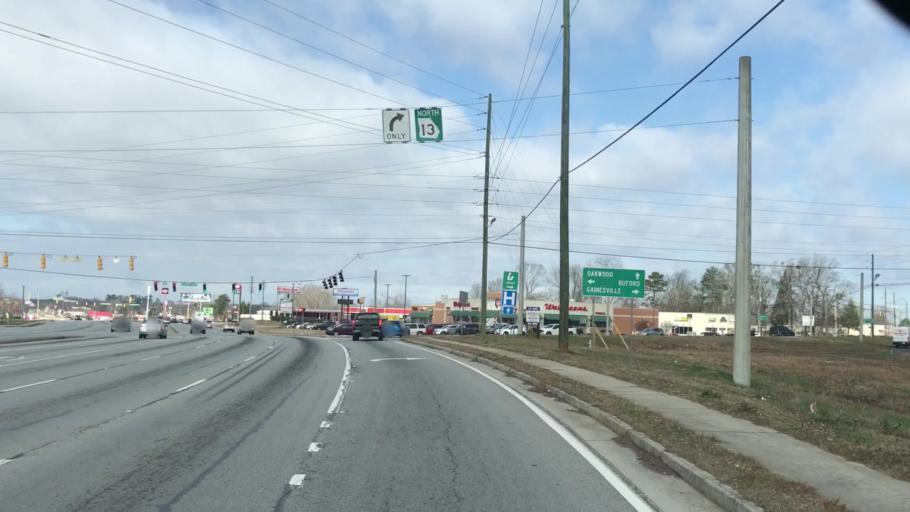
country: US
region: Georgia
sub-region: Hall County
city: Oakwood
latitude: 34.2199
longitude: -83.8619
